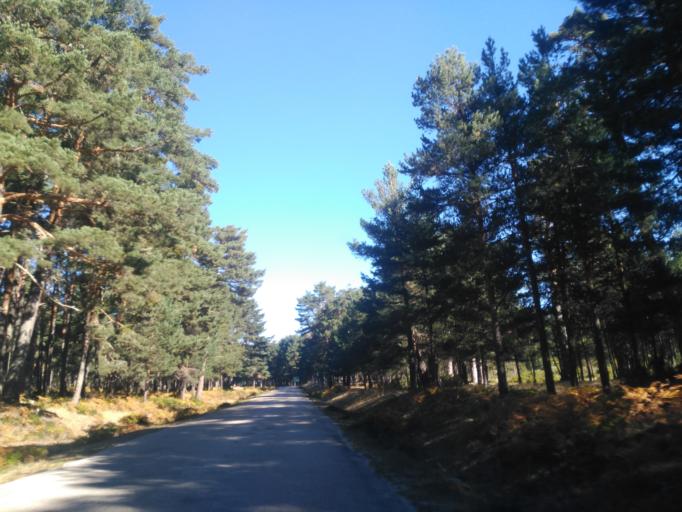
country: ES
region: Castille and Leon
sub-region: Provincia de Soria
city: Vinuesa
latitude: 41.9951
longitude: -2.8001
